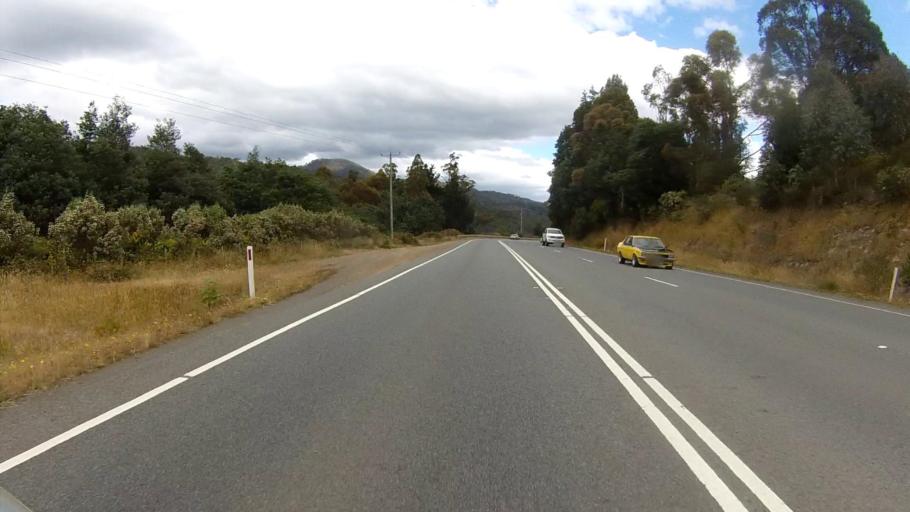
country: AU
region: Tasmania
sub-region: Huon Valley
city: Huonville
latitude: -42.9750
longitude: 147.1452
